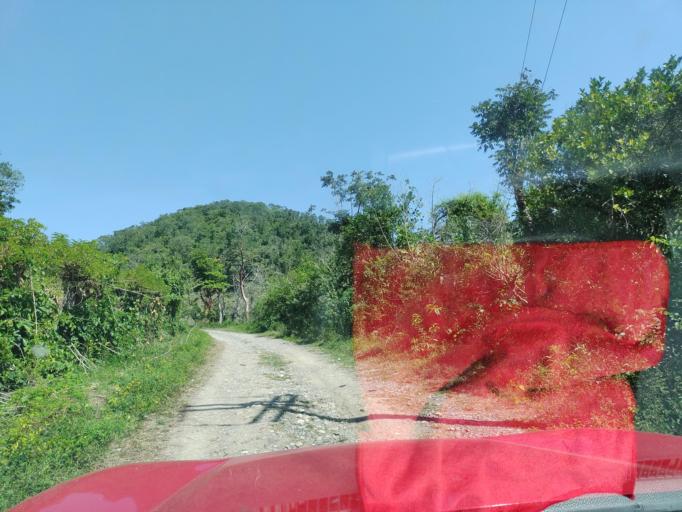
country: MX
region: Veracruz
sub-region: Papantla
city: Polutla
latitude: 20.5040
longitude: -97.2132
